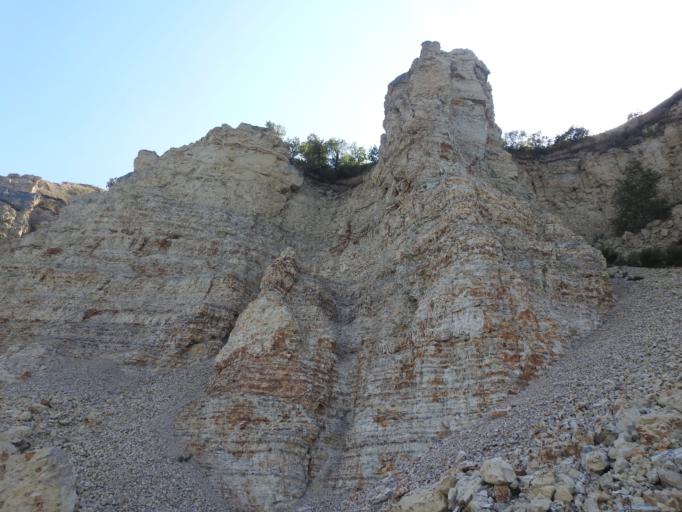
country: RU
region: Saratov
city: Rovnoye
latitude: 50.4973
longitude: 45.7952
